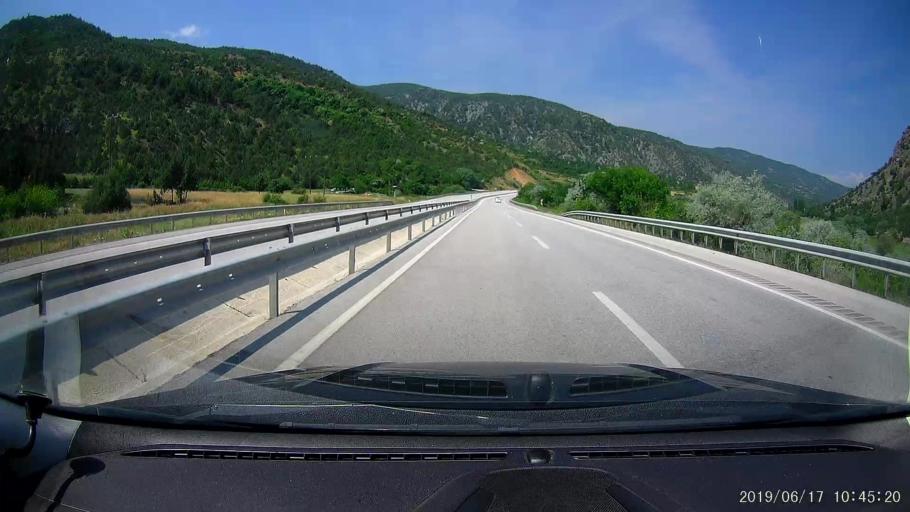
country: TR
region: Corum
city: Hacihamza
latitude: 41.0637
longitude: 34.4906
